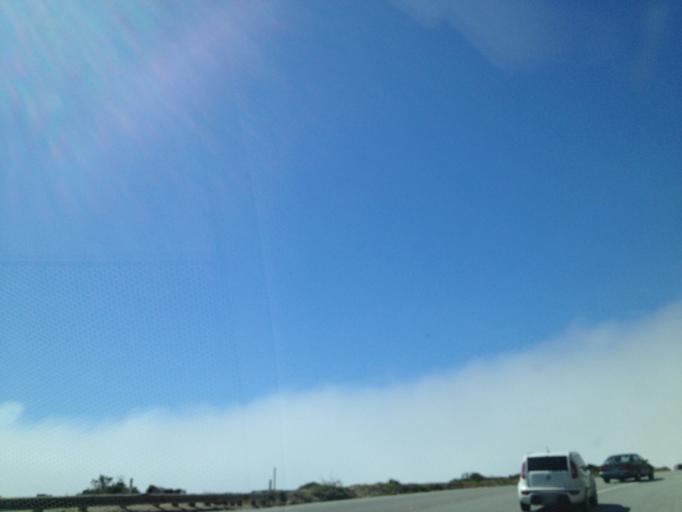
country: US
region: California
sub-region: Monterey County
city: Carmel Valley Village
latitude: 36.3524
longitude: -121.8995
